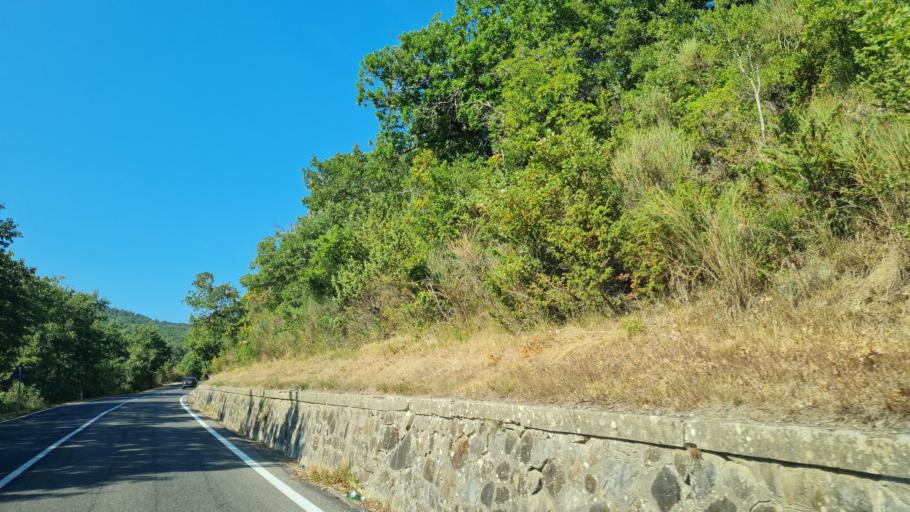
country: IT
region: Tuscany
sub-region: Provincia di Siena
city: Chianciano Terme
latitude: 43.0309
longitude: 11.7978
